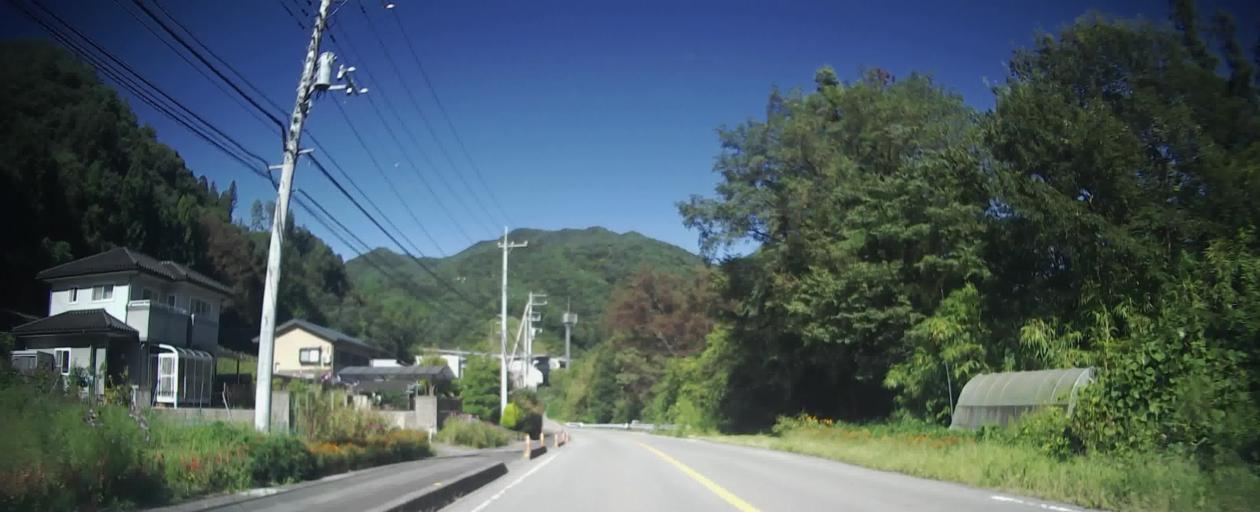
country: JP
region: Gunma
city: Nakanojomachi
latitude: 36.5697
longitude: 138.7314
